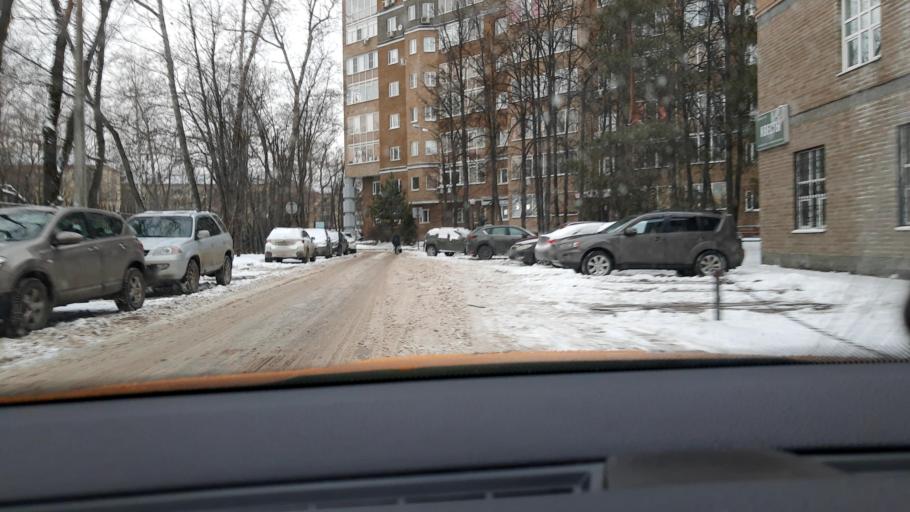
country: RU
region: Moskovskaya
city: Zhukovskiy
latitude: 55.5924
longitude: 38.1323
